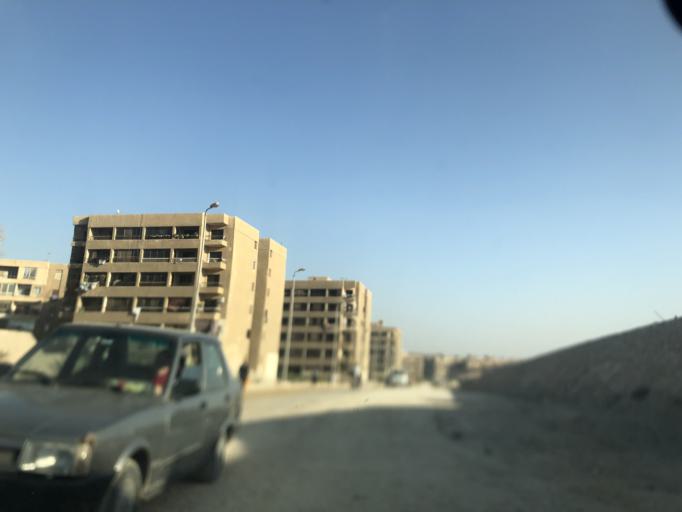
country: EG
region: Al Jizah
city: Al Jizah
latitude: 29.9900
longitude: 31.1111
